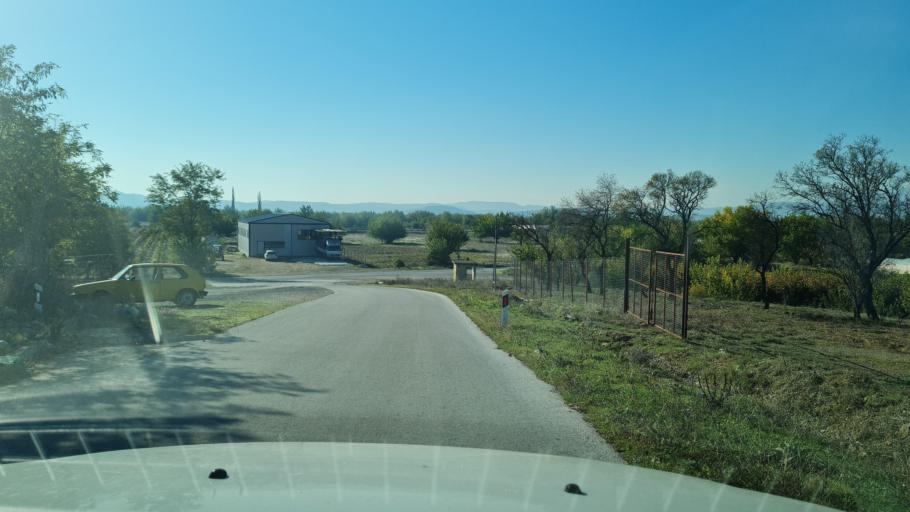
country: MK
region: Bogdanci
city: Bogdanci
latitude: 41.1932
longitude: 22.5632
